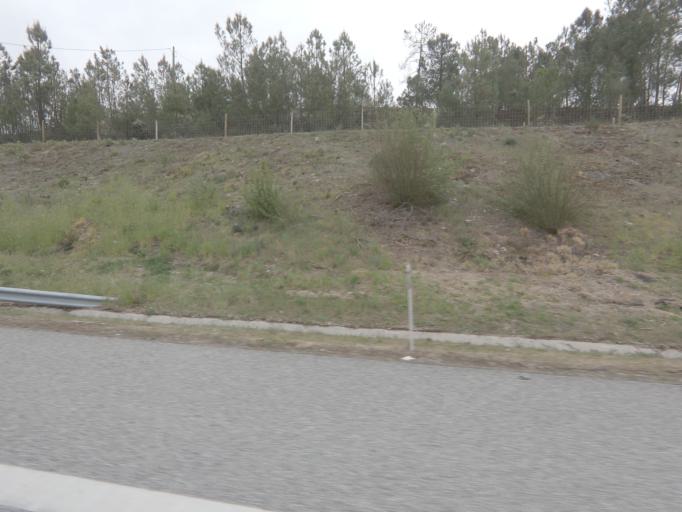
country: PT
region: Viseu
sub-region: Viseu
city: Rio de Loba
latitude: 40.6351
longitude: -7.8823
